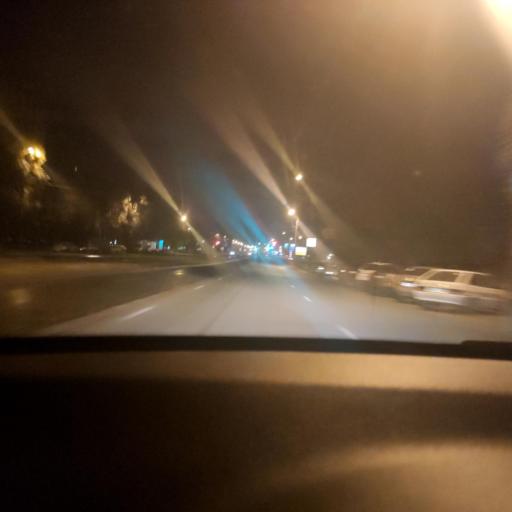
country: RU
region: Samara
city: Samara
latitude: 53.2142
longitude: 50.2253
